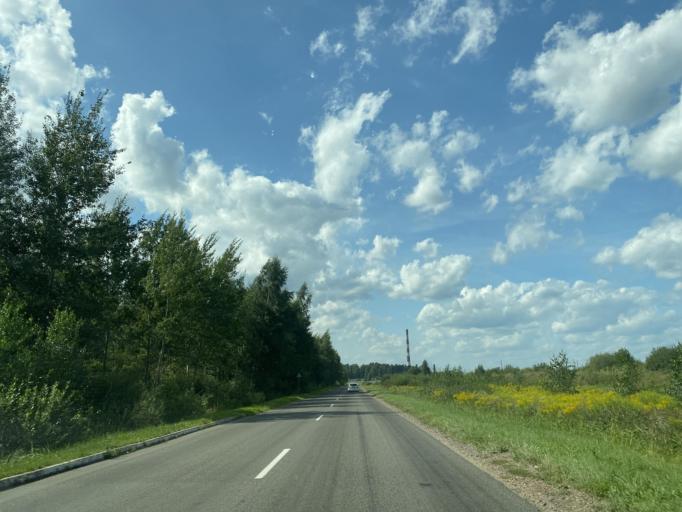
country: BY
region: Minsk
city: Horad Zhodzina
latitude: 54.0842
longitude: 28.3749
